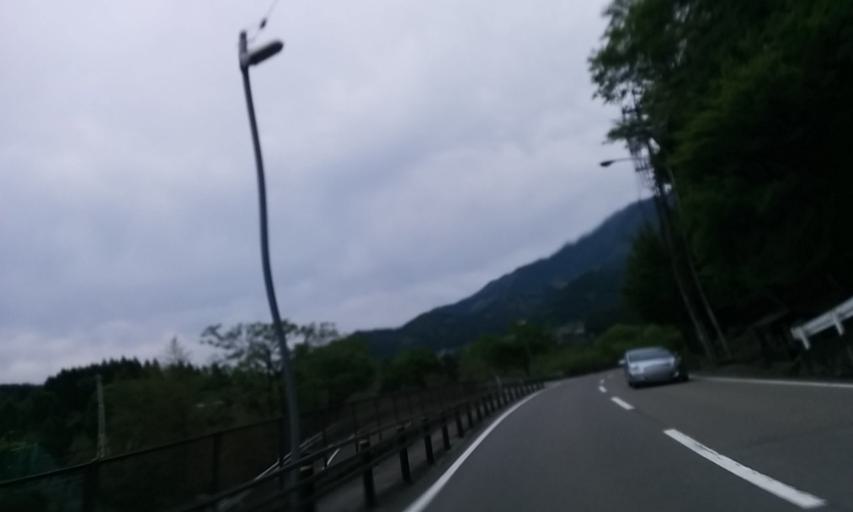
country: JP
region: Gifu
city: Gujo
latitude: 35.8162
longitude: 137.2369
